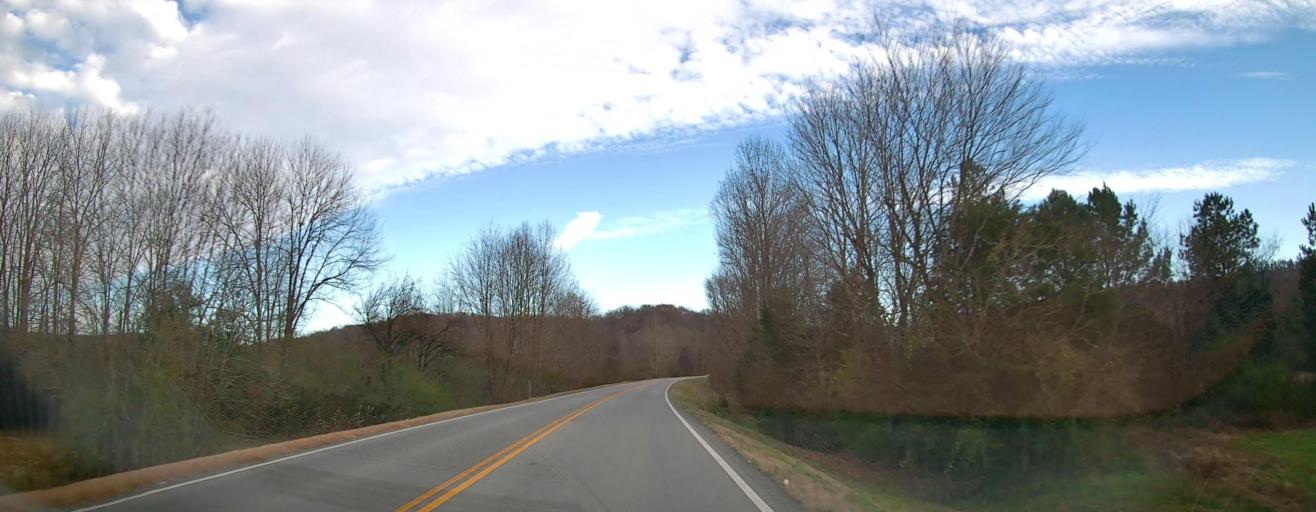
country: US
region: Alabama
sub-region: Marshall County
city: Arab
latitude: 34.3700
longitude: -86.6417
